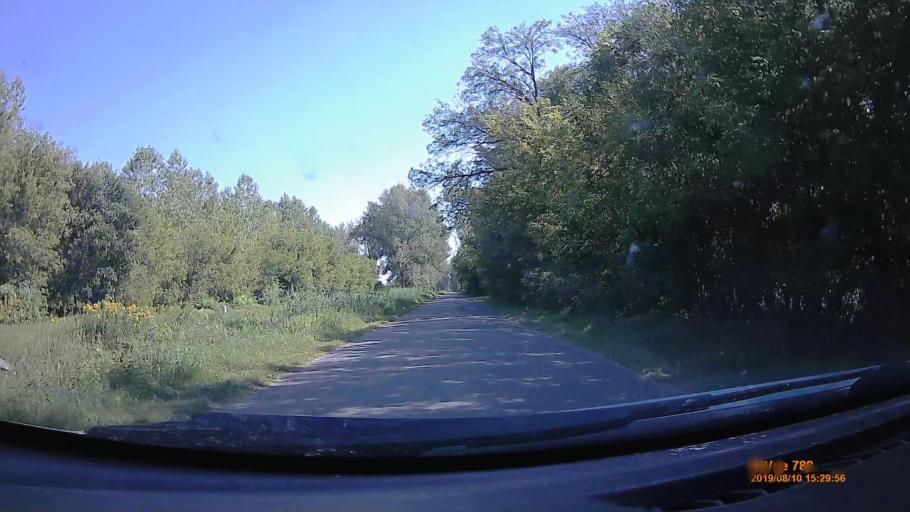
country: HU
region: Somogy
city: Balatonfenyves
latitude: 46.7021
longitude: 17.4846
